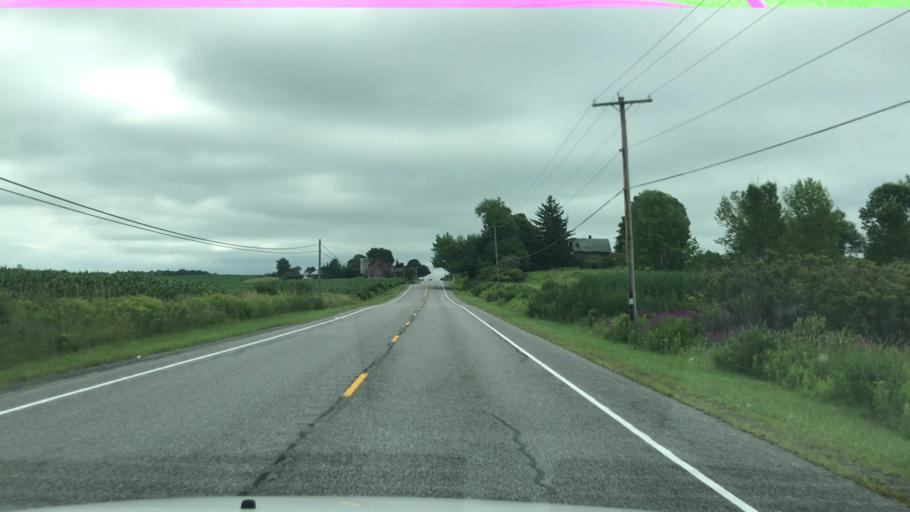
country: US
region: New York
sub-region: Wyoming County
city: Attica
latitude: 42.8361
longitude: -78.3573
